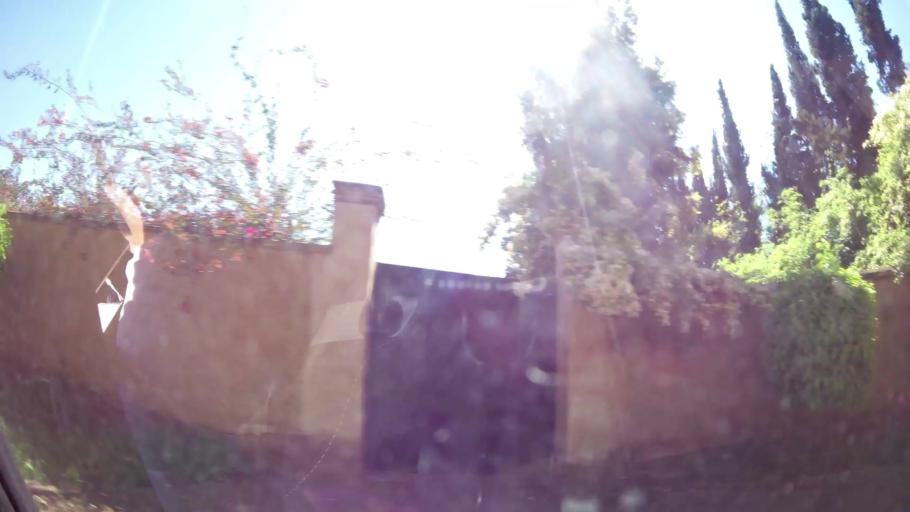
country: MA
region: Marrakech-Tensift-Al Haouz
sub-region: Marrakech
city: Marrakesh
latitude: 31.6608
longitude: -7.9585
